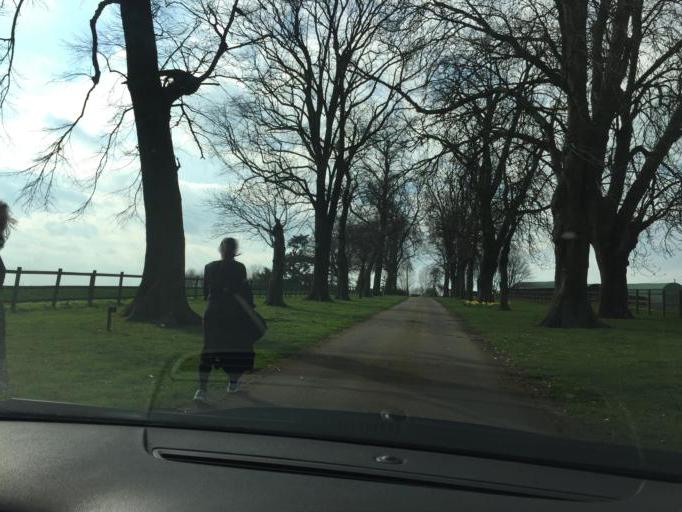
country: GB
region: England
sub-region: Solihull
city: Meriden
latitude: 52.4511
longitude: -1.5904
